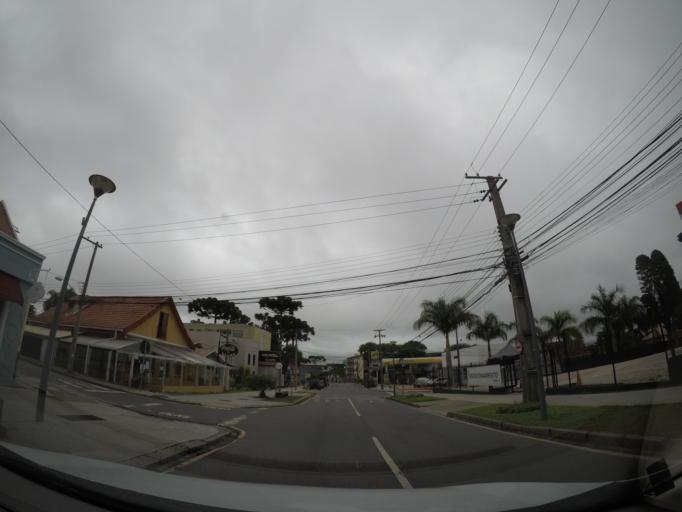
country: BR
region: Parana
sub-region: Curitiba
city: Curitiba
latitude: -25.4461
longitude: -49.2961
